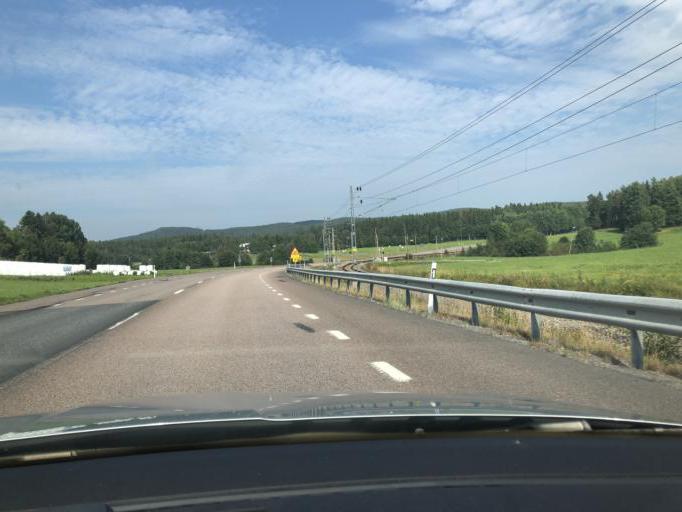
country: SE
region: Vaesternorrland
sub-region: Kramfors Kommun
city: Kramfors
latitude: 62.8238
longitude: 17.8479
